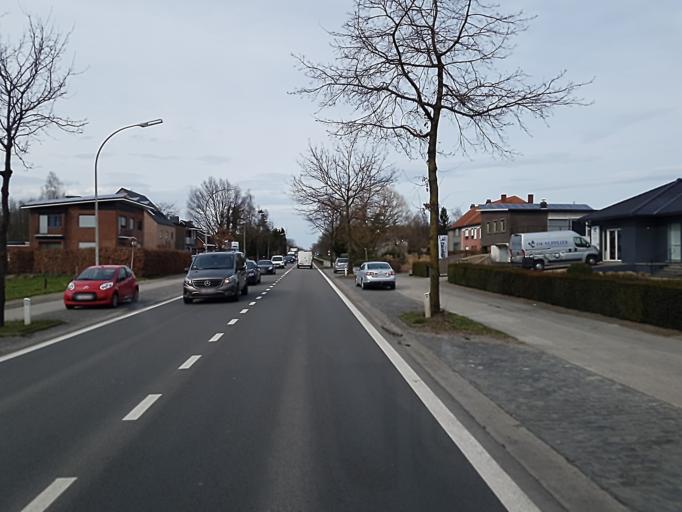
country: BE
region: Flanders
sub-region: Provincie Antwerpen
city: Mol
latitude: 51.2117
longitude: 5.1154
